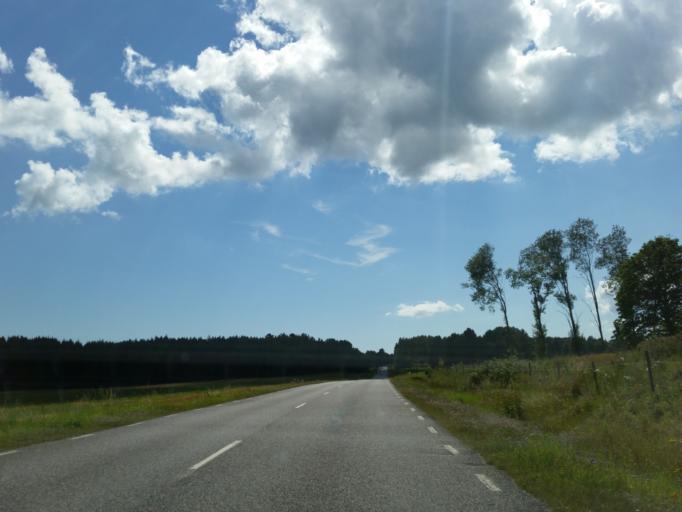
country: SE
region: Stockholm
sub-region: Sodertalje Kommun
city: Pershagen
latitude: 59.0305
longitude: 17.6745
